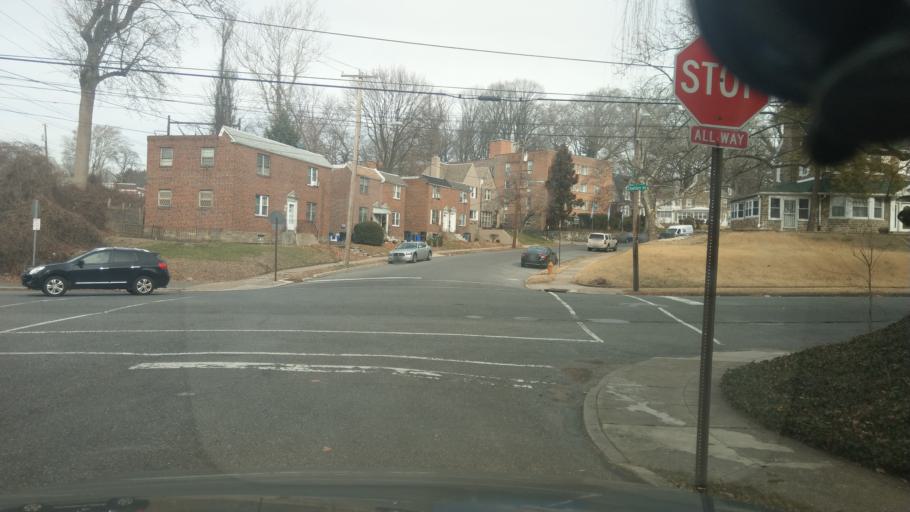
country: US
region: Pennsylvania
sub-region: Montgomery County
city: Wyncote
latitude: 40.0487
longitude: -75.1345
